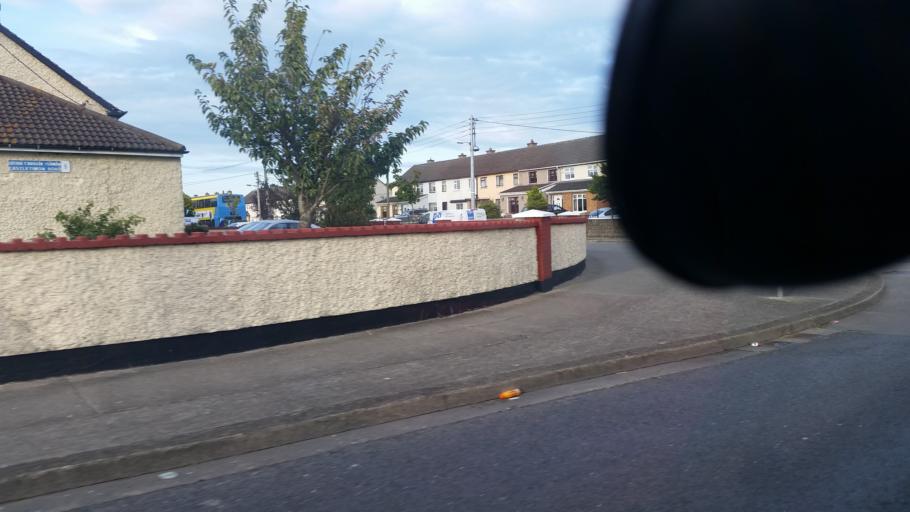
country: IE
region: Leinster
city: Artane
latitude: 53.3951
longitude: -6.2258
